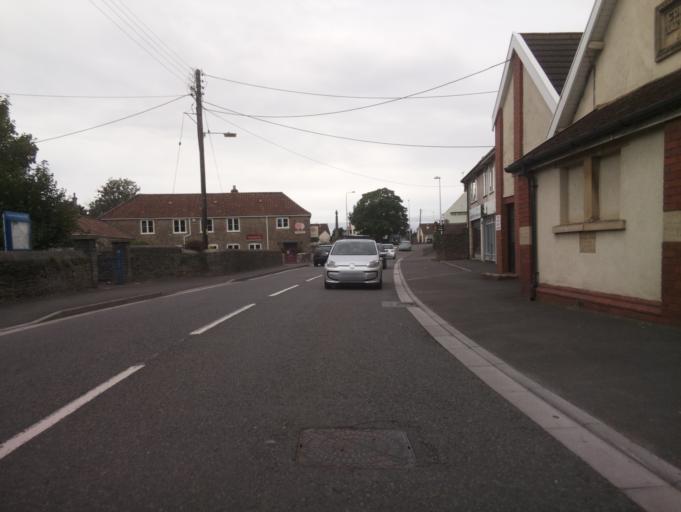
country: GB
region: England
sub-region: North Somerset
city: Congresbury
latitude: 51.3702
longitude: -2.8091
